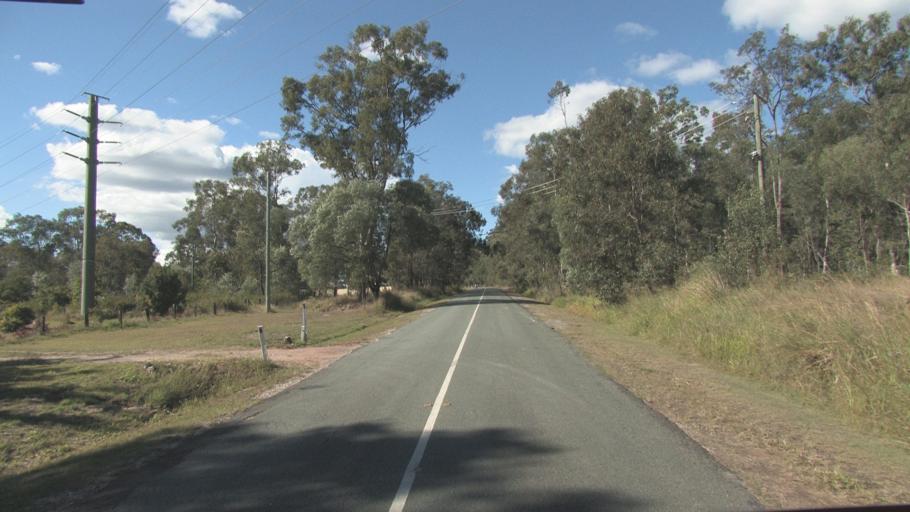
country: AU
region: Queensland
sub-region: Logan
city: Chambers Flat
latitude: -27.7896
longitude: 153.0956
